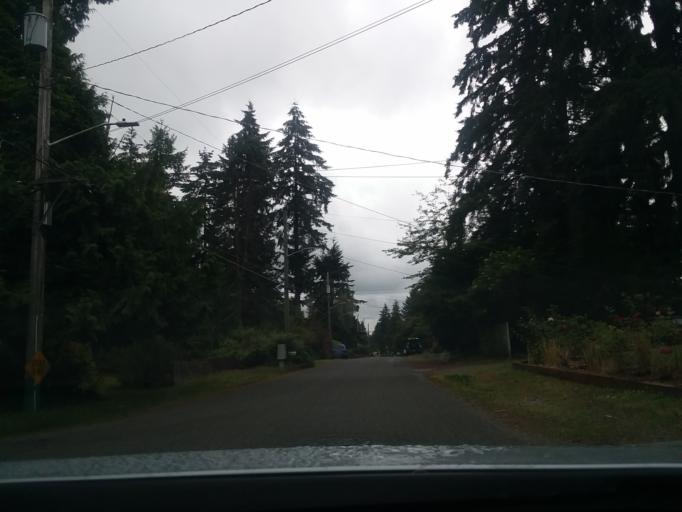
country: US
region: Washington
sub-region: King County
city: Lake Forest Park
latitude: 47.7331
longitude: -122.2992
